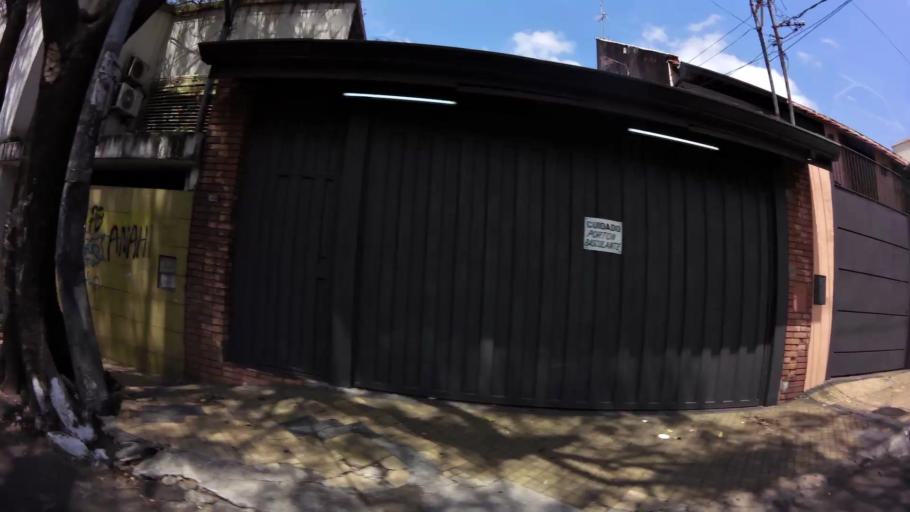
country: PY
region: Asuncion
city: Asuncion
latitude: -25.2856
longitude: -57.6444
